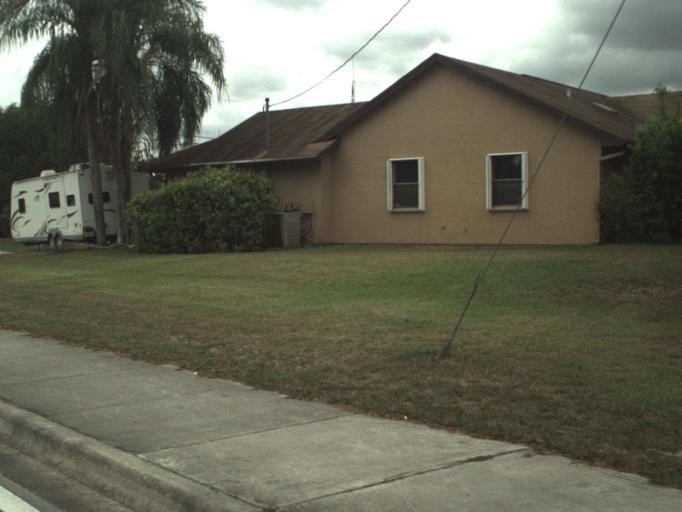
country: US
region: Florida
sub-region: Saint Lucie County
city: Port Saint Lucie
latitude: 27.2770
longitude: -80.3421
